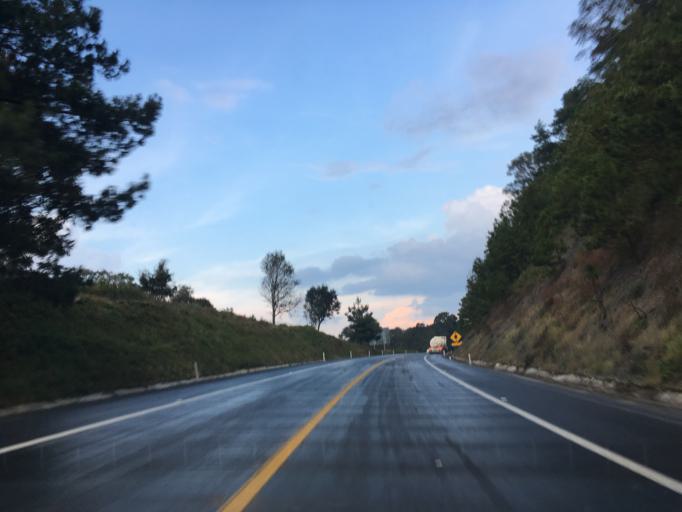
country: MX
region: Michoacan
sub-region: Patzcuaro
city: Santa Maria Huiramangaro (San Juan Tumbio)
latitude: 19.4856
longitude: -101.7237
